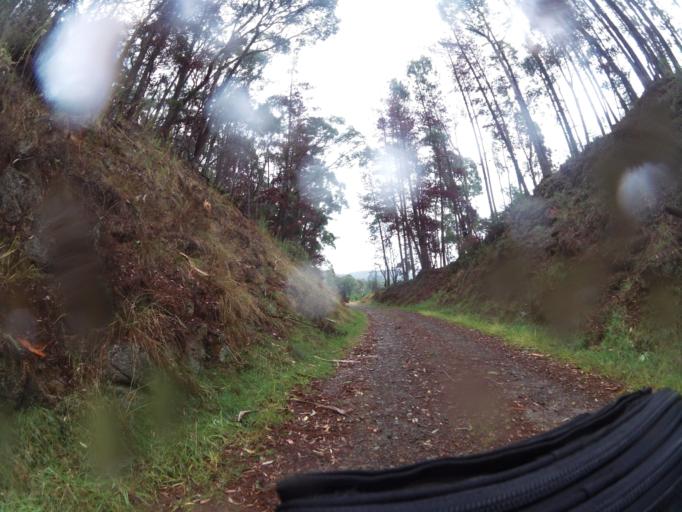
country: AU
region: New South Wales
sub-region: Greater Hume Shire
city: Holbrook
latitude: -36.2245
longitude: 147.5779
